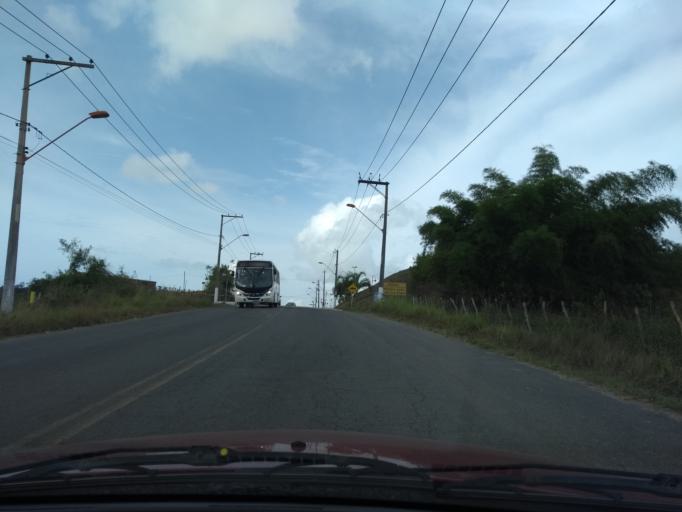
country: BR
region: Bahia
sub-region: Sao Francisco Do Conde
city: Sao Francisco do Conde
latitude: -12.6113
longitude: -38.6535
